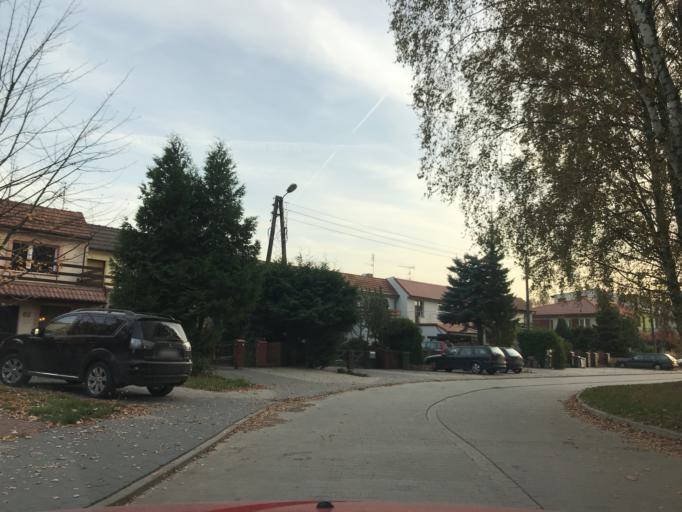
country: PL
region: Greater Poland Voivodeship
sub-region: Powiat poznanski
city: Plewiska
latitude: 52.3934
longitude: 16.7973
